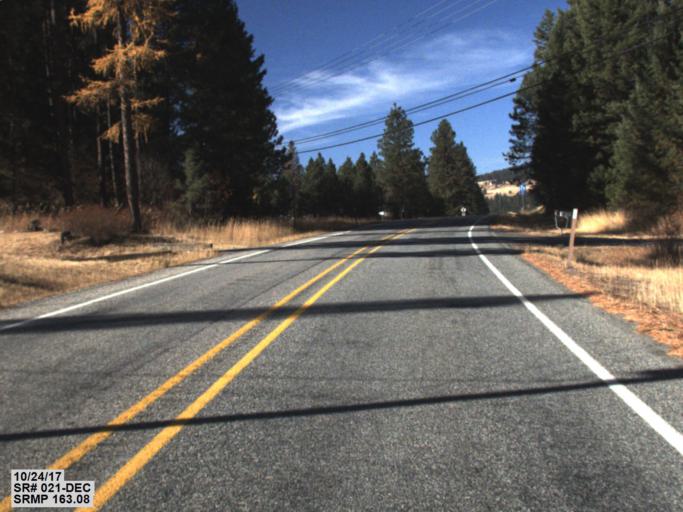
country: US
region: Washington
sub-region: Ferry County
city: Republic
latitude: 48.6504
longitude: -118.6768
